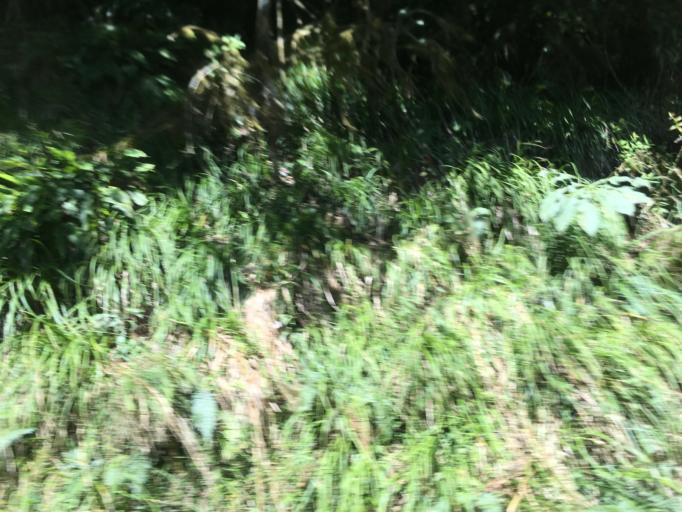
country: TW
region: Taiwan
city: Daxi
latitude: 24.6103
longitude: 121.4595
